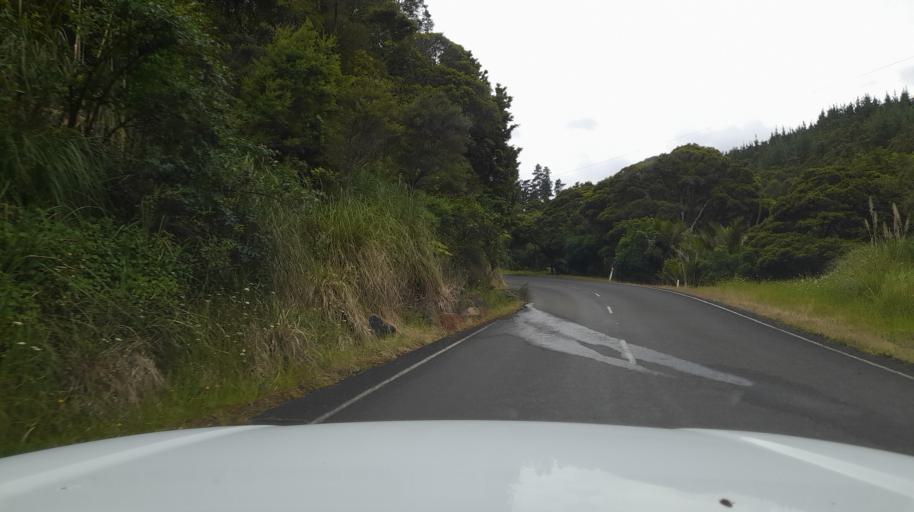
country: NZ
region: Northland
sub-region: Far North District
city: Kaitaia
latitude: -35.3625
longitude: 173.3963
